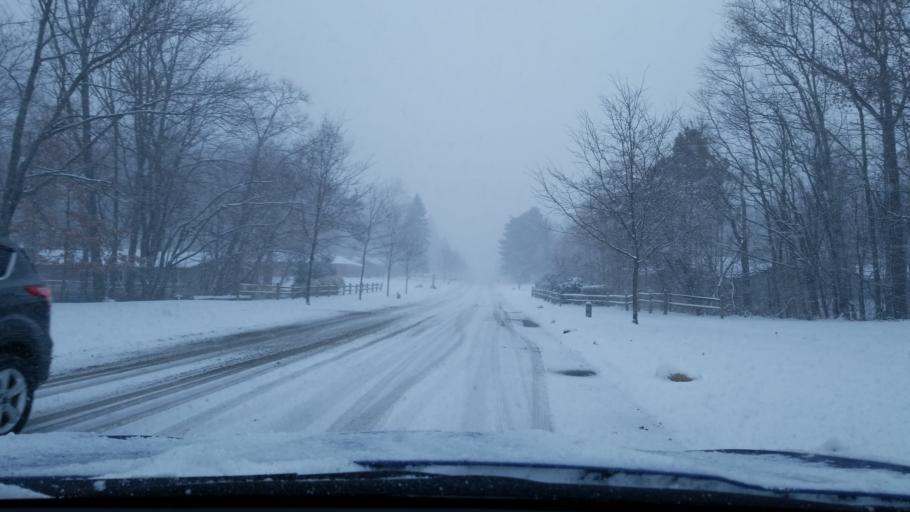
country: US
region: Ohio
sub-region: Cuyahoga County
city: Strongsville
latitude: 41.3169
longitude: -81.8210
